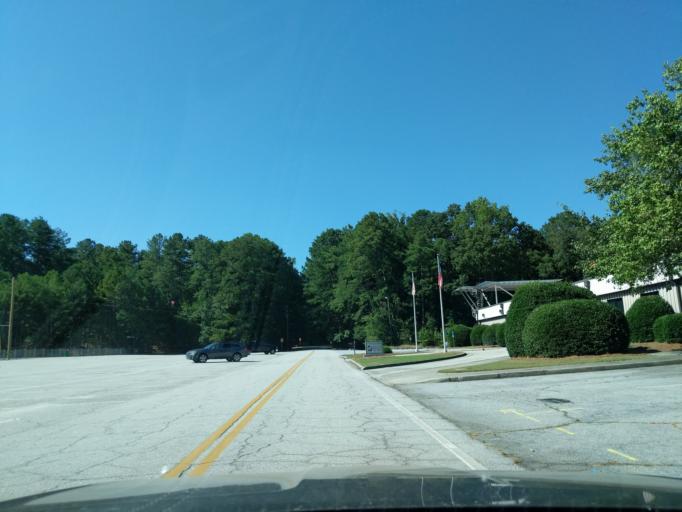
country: US
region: Georgia
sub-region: DeKalb County
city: Stone Mountain
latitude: 33.8184
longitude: -84.1507
